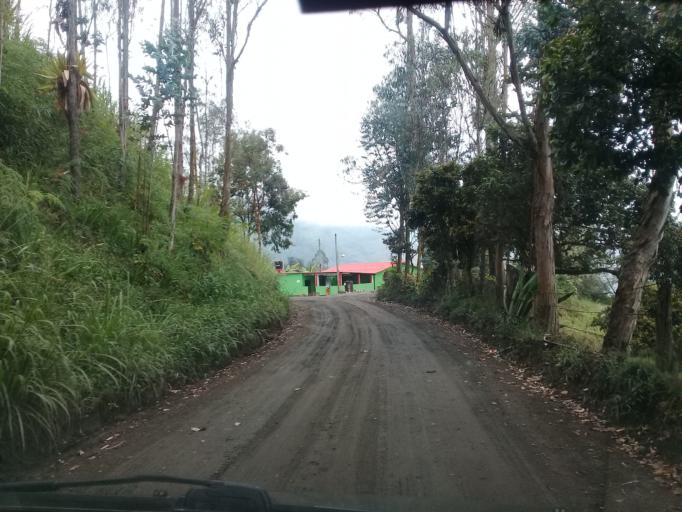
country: CO
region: Cundinamarca
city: Caqueza
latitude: 4.3958
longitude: -73.9815
